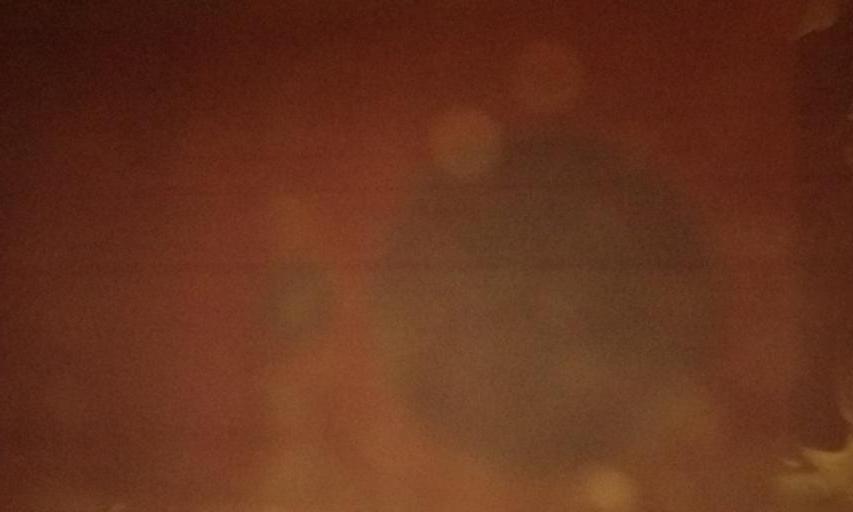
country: JP
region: Hyogo
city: Himeji
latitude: 34.8293
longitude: 134.6609
